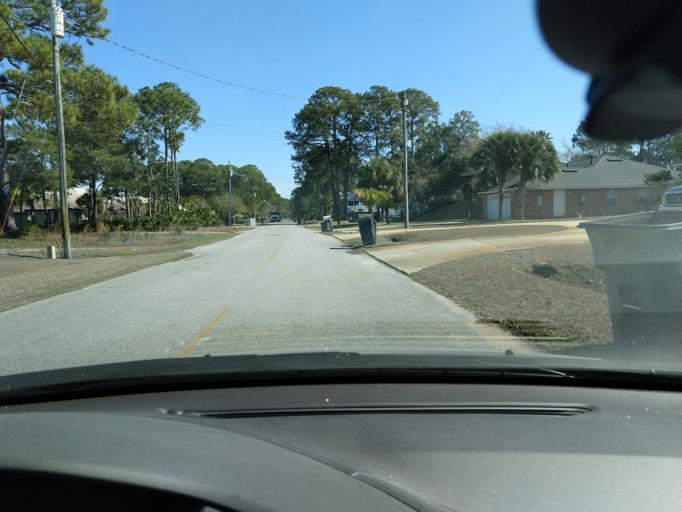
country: US
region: Florida
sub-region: Walton County
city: Miramar Beach
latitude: 30.3900
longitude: -86.3772
